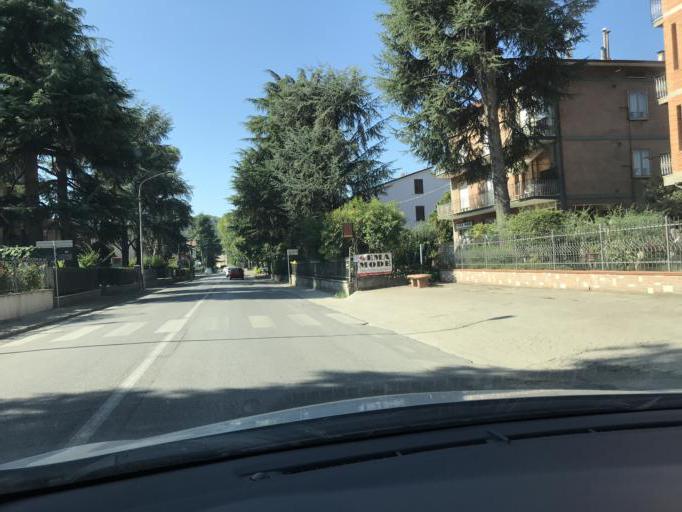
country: IT
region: Umbria
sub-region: Provincia di Perugia
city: Ponte Felcino
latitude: 43.1127
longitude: 12.4509
